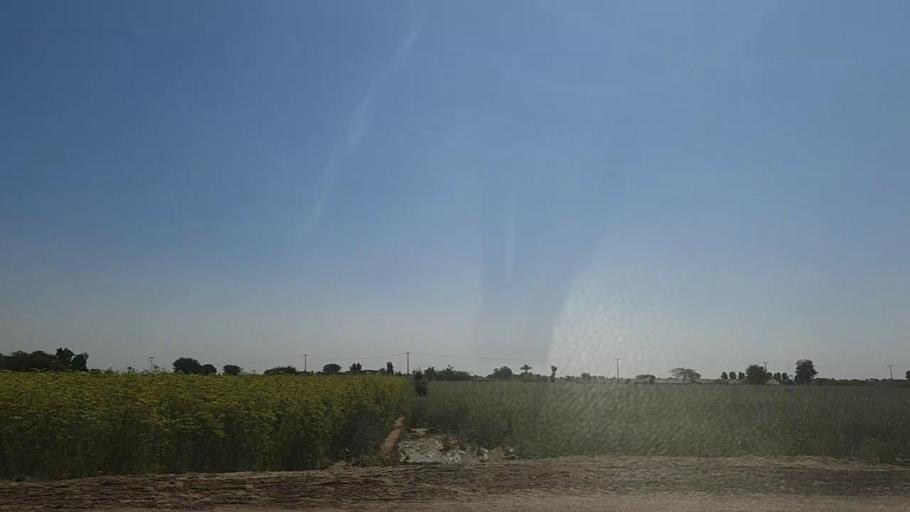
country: PK
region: Sindh
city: Kunri
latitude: 25.2823
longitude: 69.5206
